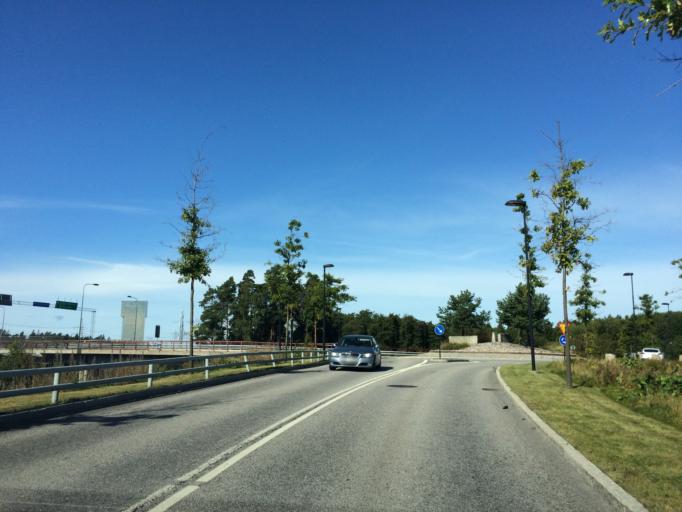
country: SE
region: Stockholm
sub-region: Stockholms Kommun
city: Kista
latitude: 59.4024
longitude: 17.9756
